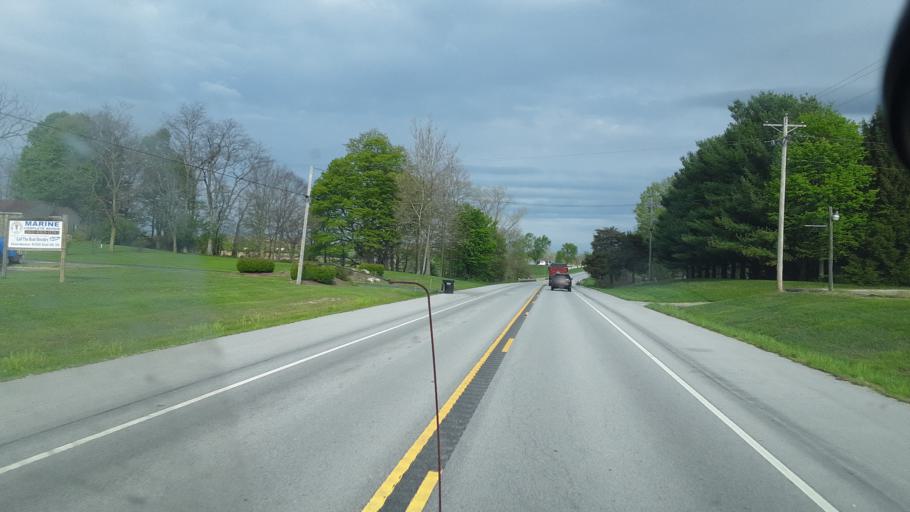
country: US
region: Indiana
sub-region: Whitley County
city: Churubusco
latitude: 41.2576
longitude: -85.3692
